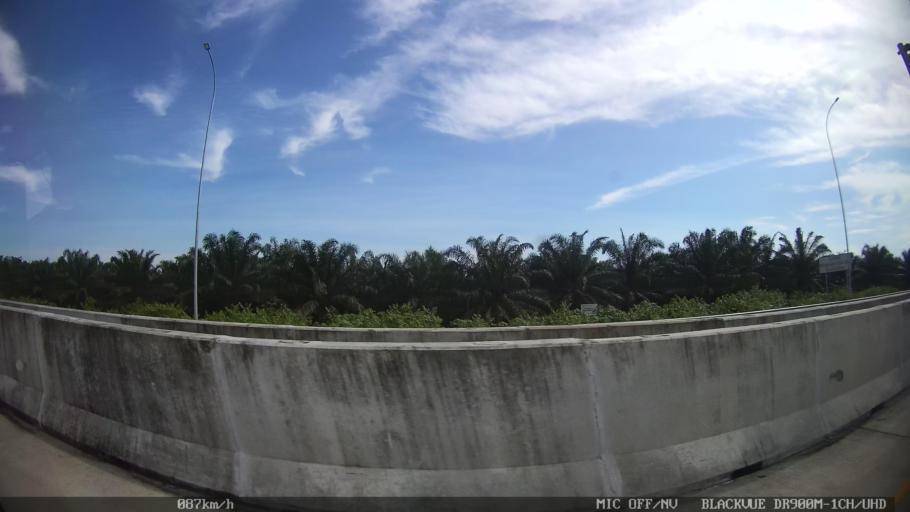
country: ID
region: North Sumatra
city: Binjai
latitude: 3.6492
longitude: 98.5428
